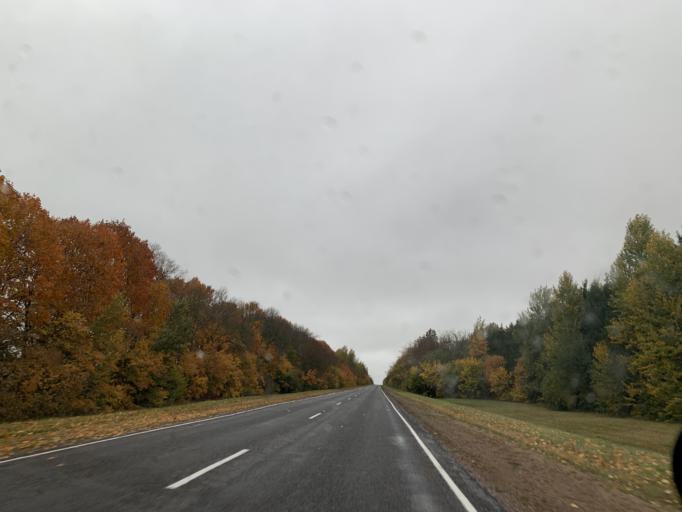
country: BY
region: Minsk
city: Haradzyeya
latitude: 53.3861
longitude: 26.5664
